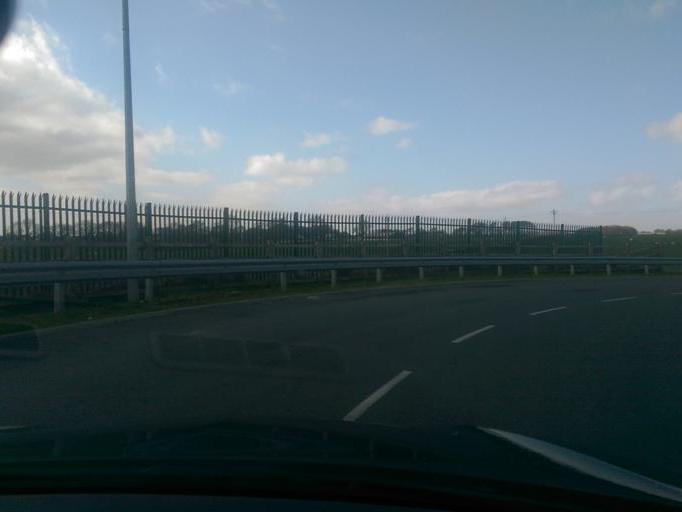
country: IE
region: Connaught
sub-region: County Galway
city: Athenry
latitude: 53.2866
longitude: -8.7616
